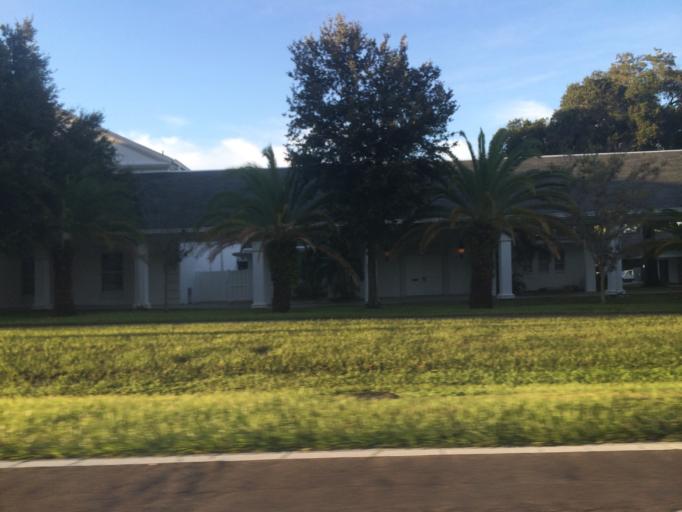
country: US
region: Florida
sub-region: Pinellas County
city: Largo
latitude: 27.9424
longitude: -82.7685
